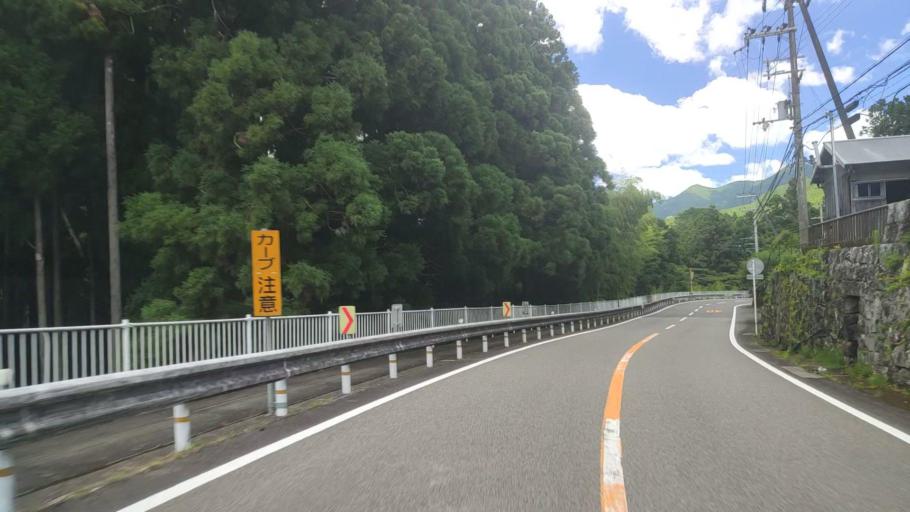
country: JP
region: Mie
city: Owase
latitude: 33.9524
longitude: 136.0687
